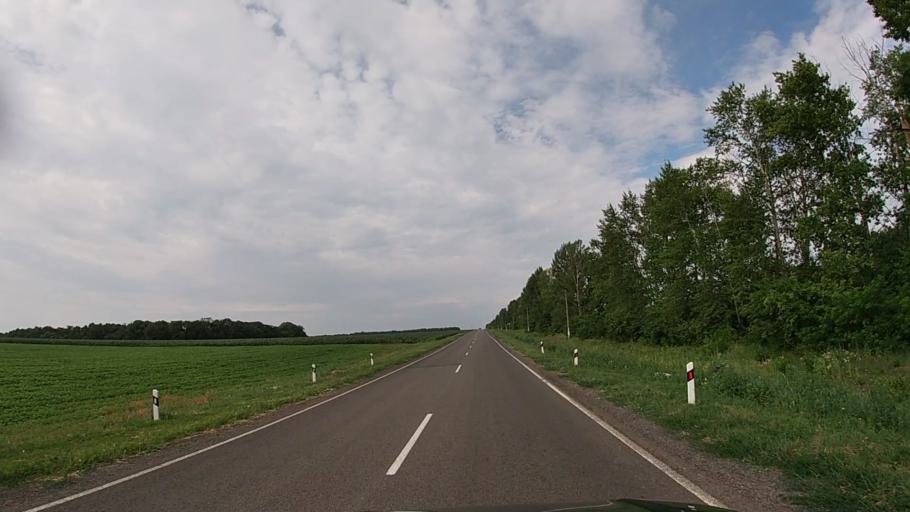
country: RU
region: Belgorod
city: Krasnaya Yaruga
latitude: 50.8291
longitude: 35.4758
